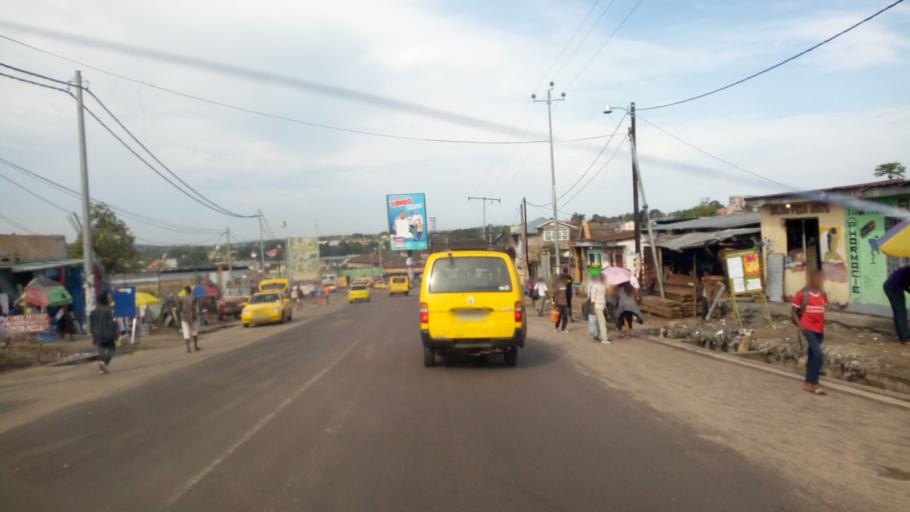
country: CD
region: Kinshasa
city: Kinshasa
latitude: -4.4435
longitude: 15.2544
